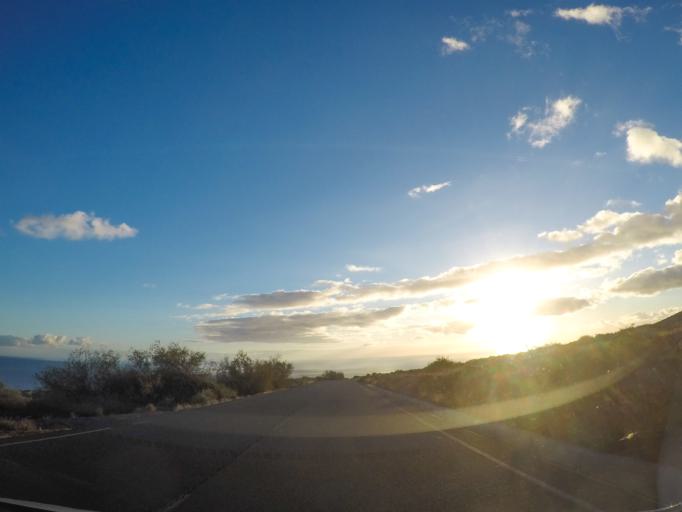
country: ES
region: Canary Islands
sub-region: Provincia de Santa Cruz de Tenerife
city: Alajero
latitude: 28.0357
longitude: -17.2202
